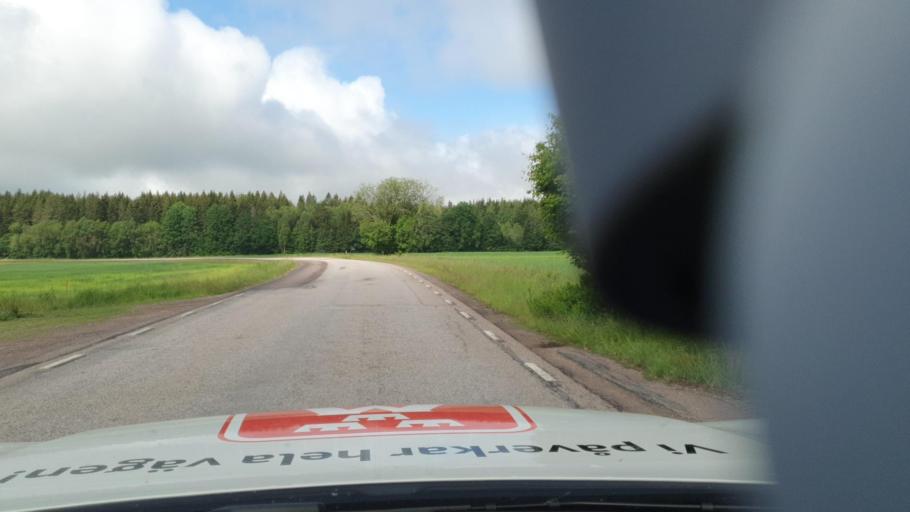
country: SE
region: Vaermland
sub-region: Kristinehamns Kommun
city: Bjorneborg
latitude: 59.0997
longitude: 14.2971
